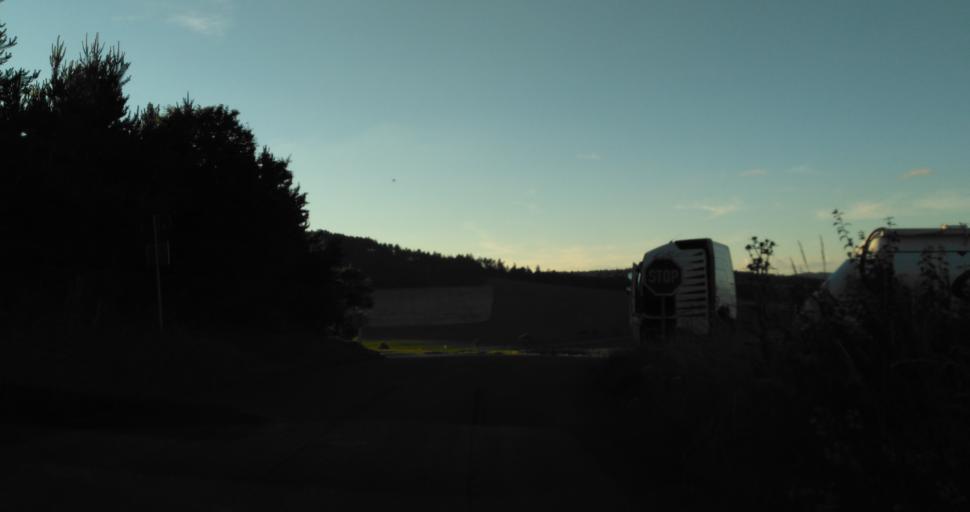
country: CZ
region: Central Bohemia
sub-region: Okres Beroun
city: Kraluv Dvur
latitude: 49.9130
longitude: 14.0334
